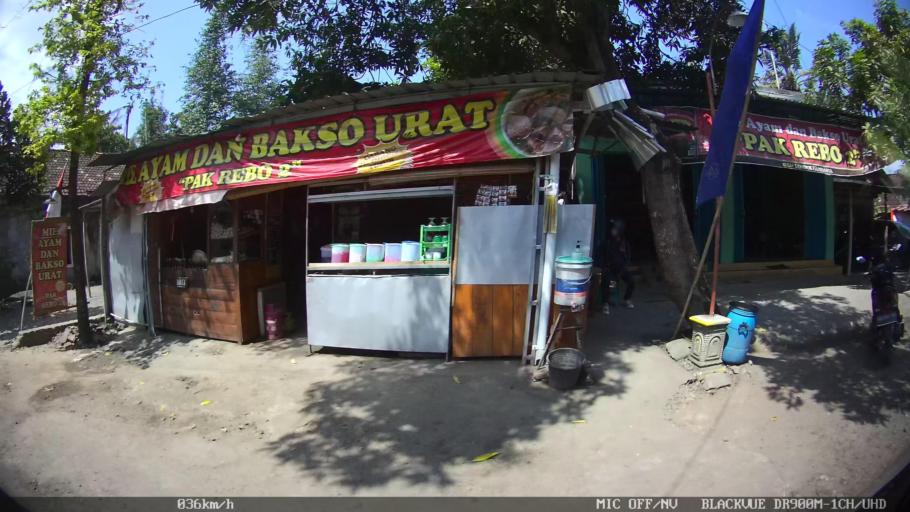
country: ID
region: Daerah Istimewa Yogyakarta
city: Pundong
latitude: -7.9434
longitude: 110.3744
